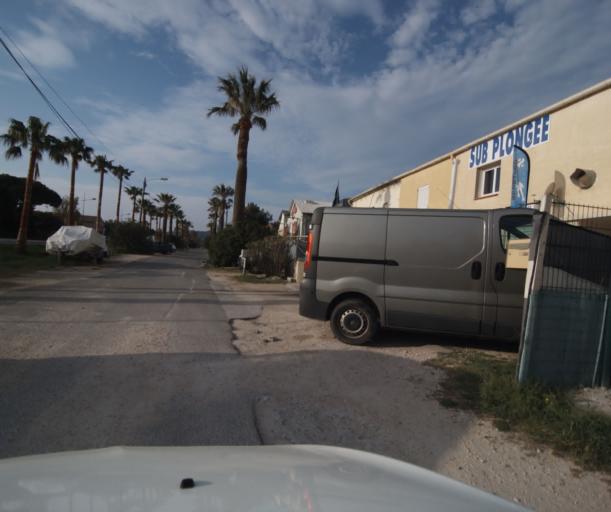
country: FR
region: Provence-Alpes-Cote d'Azur
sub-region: Departement du Var
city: Hyeres
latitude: 43.0496
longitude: 6.1465
